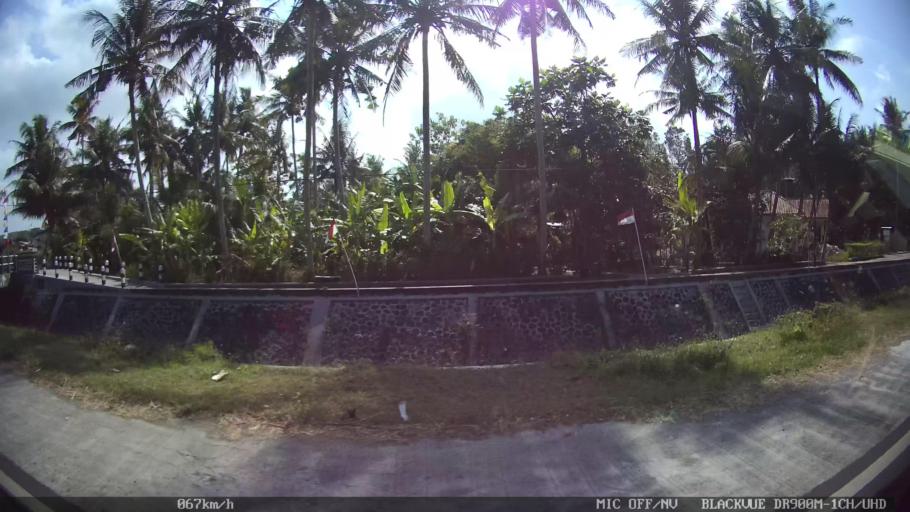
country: ID
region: Daerah Istimewa Yogyakarta
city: Srandakan
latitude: -7.9008
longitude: 110.1663
